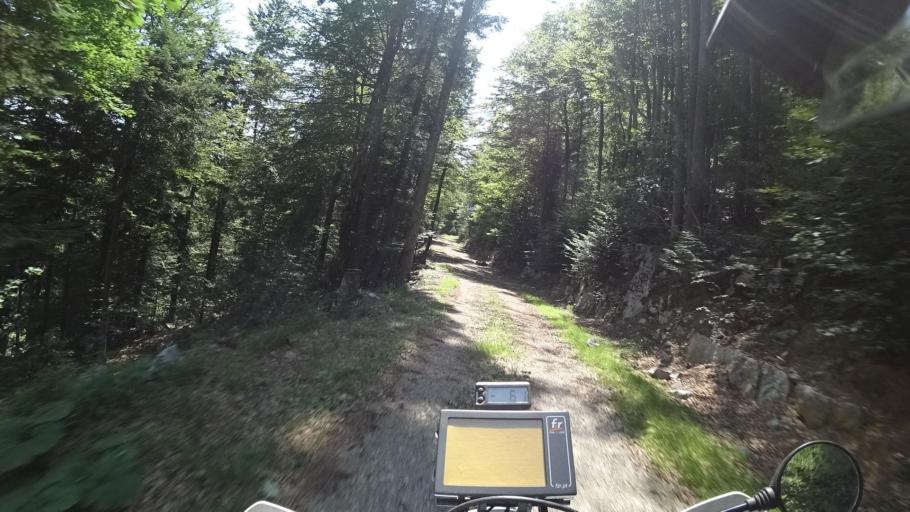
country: HR
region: Primorsko-Goranska
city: Bribir
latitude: 45.2606
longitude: 14.8633
